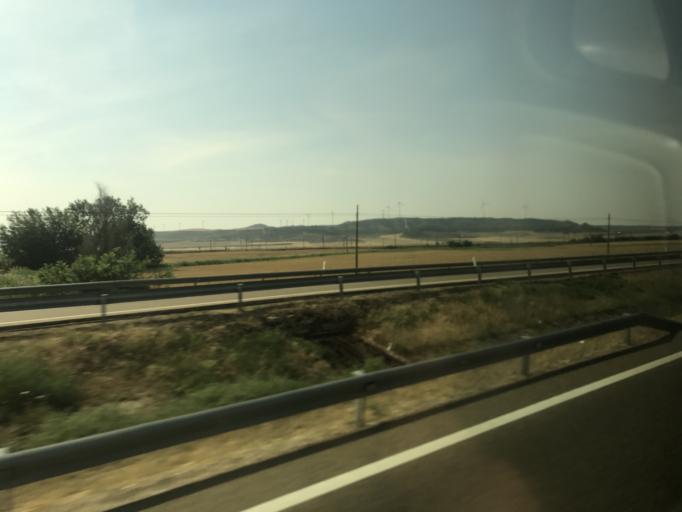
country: ES
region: Castille and Leon
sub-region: Provincia de Palencia
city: Cordovilla la Real
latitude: 42.0613
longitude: -4.2333
